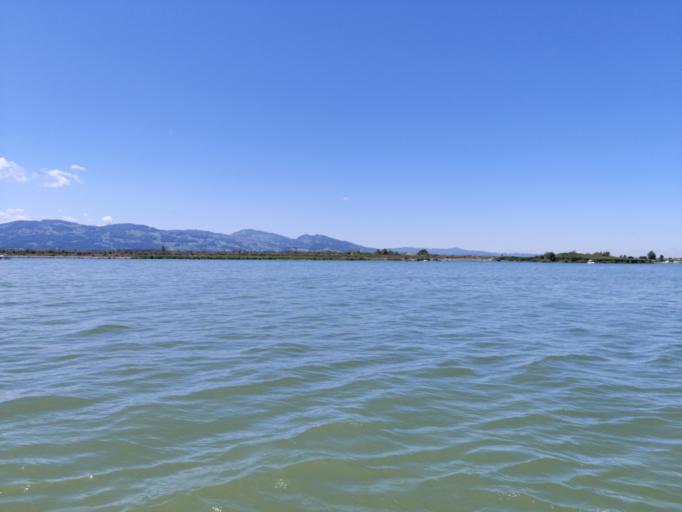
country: AT
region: Vorarlberg
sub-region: Politischer Bezirk Bregenz
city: Hard
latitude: 47.5131
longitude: 9.6675
